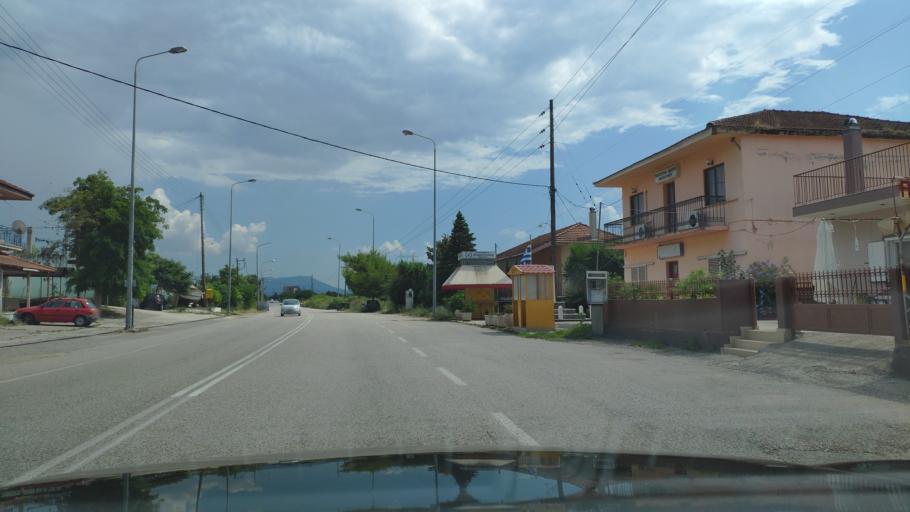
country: GR
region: West Greece
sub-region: Nomos Aitolias kai Akarnanias
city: Krikellos
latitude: 38.9714
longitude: 21.1675
